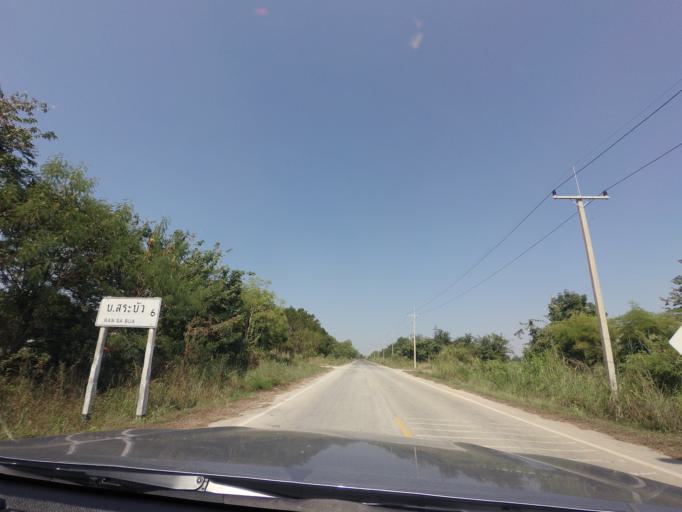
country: TH
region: Sukhothai
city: Sukhothai
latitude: 17.0696
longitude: 99.7921
